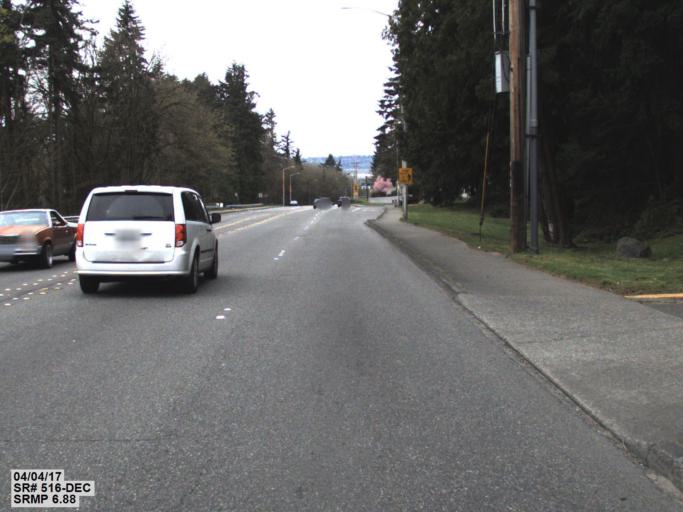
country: US
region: Washington
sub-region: King County
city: Kent
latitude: 47.3747
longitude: -122.2111
